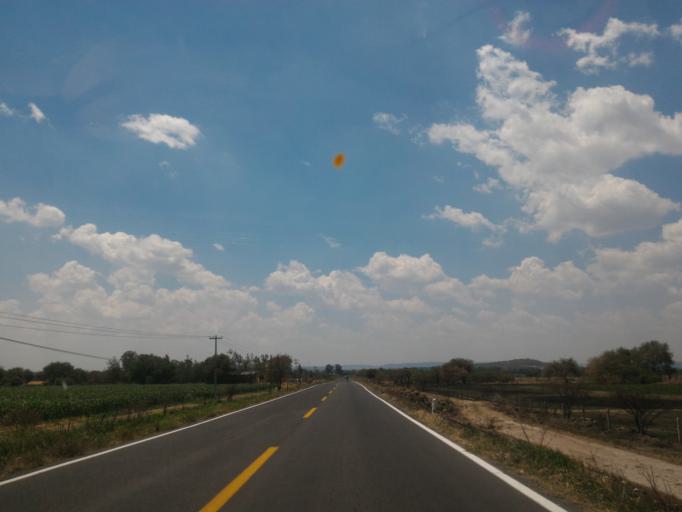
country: MX
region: Guanajuato
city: Ciudad Manuel Doblado
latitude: 20.7778
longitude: -101.9770
